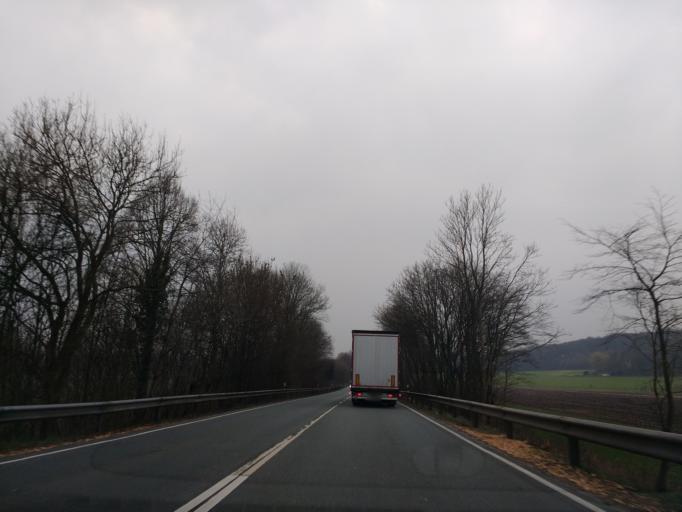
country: DE
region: North Rhine-Westphalia
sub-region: Regierungsbezirk Munster
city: Lotte
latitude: 52.2684
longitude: 7.8947
